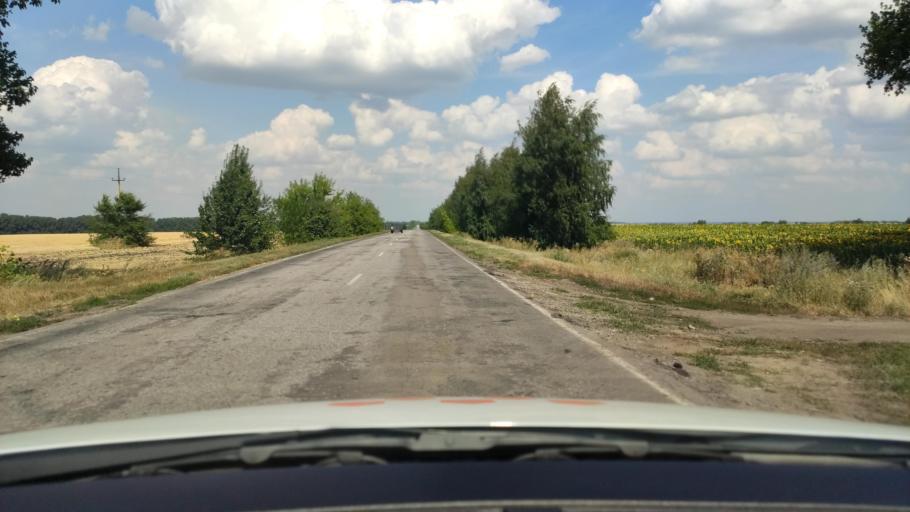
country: RU
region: Voronezj
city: Pereleshinskiy
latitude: 51.7358
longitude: 40.3887
